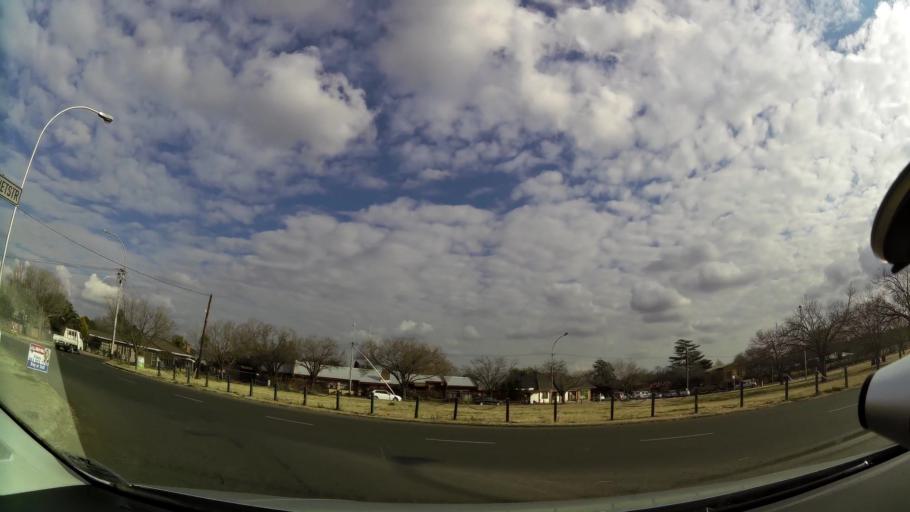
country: ZA
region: Orange Free State
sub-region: Mangaung Metropolitan Municipality
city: Bloemfontein
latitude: -29.0825
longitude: 26.2150
